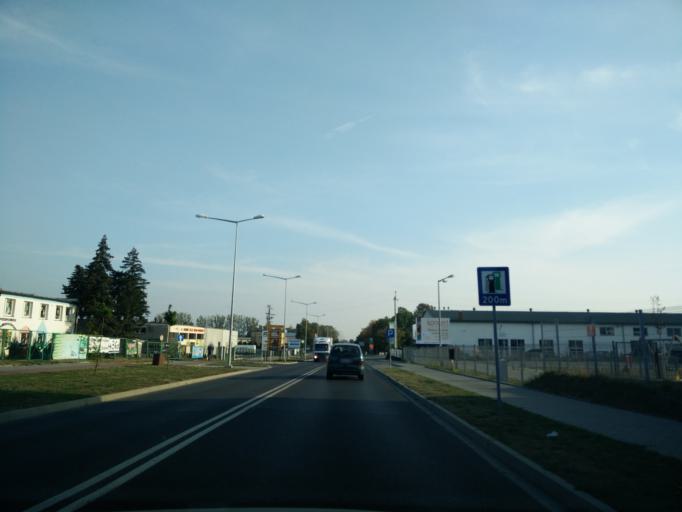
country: PL
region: Greater Poland Voivodeship
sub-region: Powiat sredzki
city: Sroda Wielkopolska
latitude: 52.2216
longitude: 17.2871
